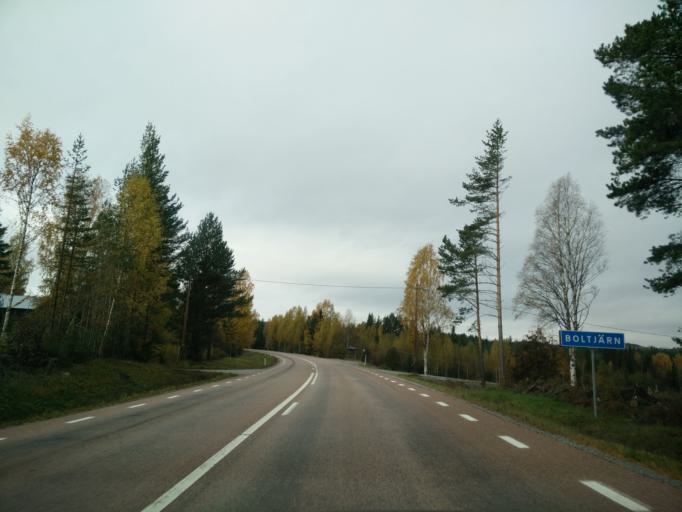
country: SE
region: Vaesternorrland
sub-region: Ange Kommun
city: Ange
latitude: 62.5385
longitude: 15.7170
